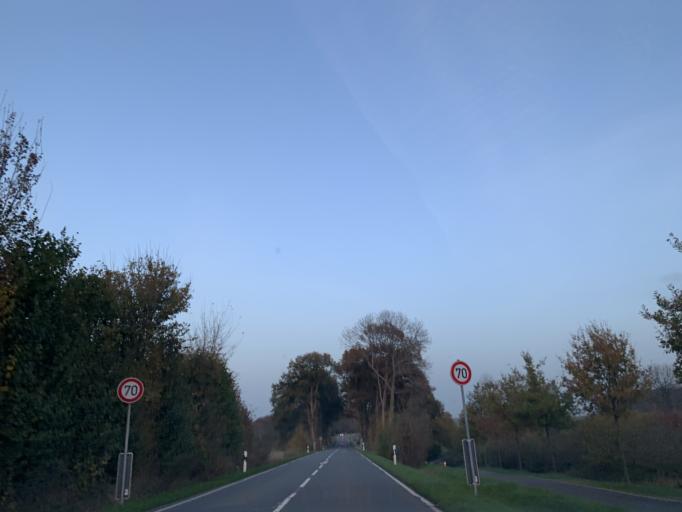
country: DE
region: North Rhine-Westphalia
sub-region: Regierungsbezirk Munster
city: Nottuln
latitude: 51.9810
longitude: 7.3623
